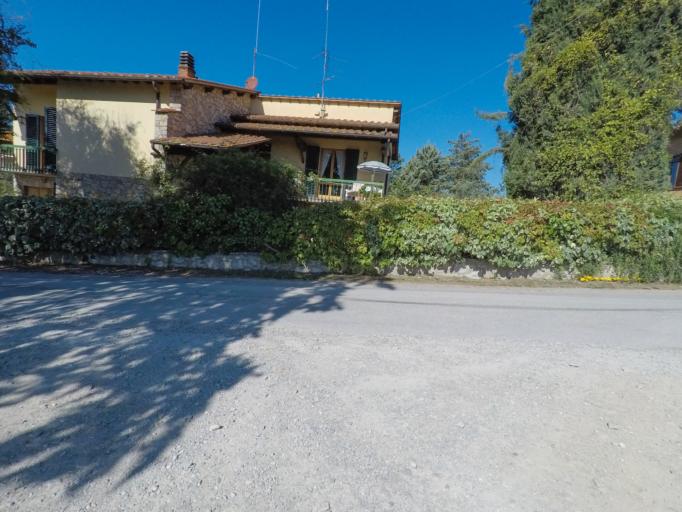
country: IT
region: Tuscany
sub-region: Provincia di Siena
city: Castellina in Chianti
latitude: 43.4358
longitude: 11.3074
